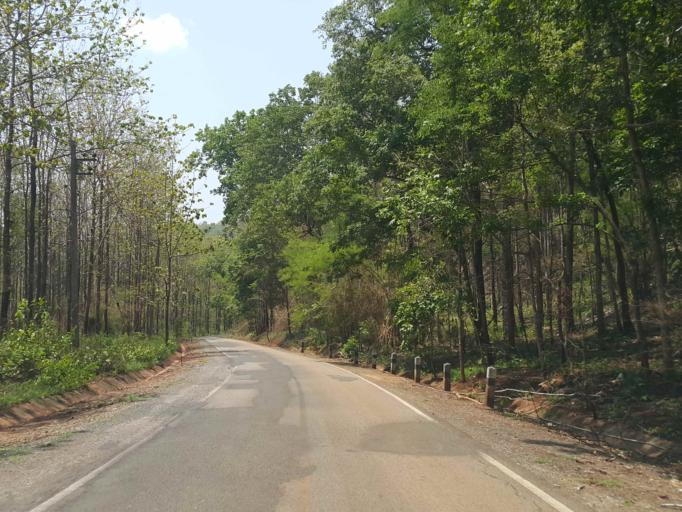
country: TH
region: Chiang Mai
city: Mae Taeng
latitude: 19.0776
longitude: 99.0868
